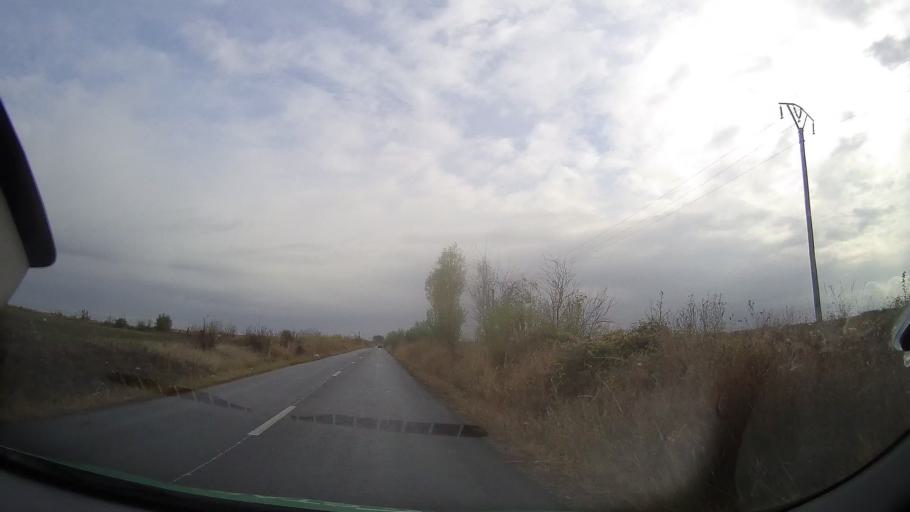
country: RO
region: Ialomita
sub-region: Comuna Maia
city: Maia
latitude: 44.7499
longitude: 26.3917
